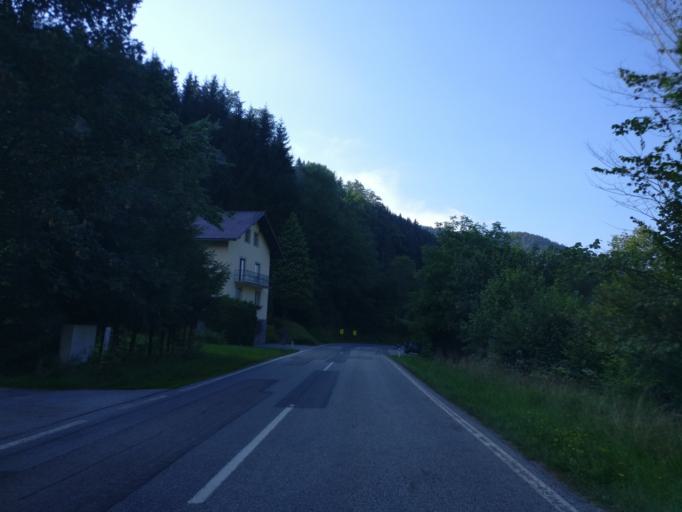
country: AT
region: Lower Austria
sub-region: Politischer Bezirk Scheibbs
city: Gostling an der Ybbs
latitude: 47.7727
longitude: 14.9057
